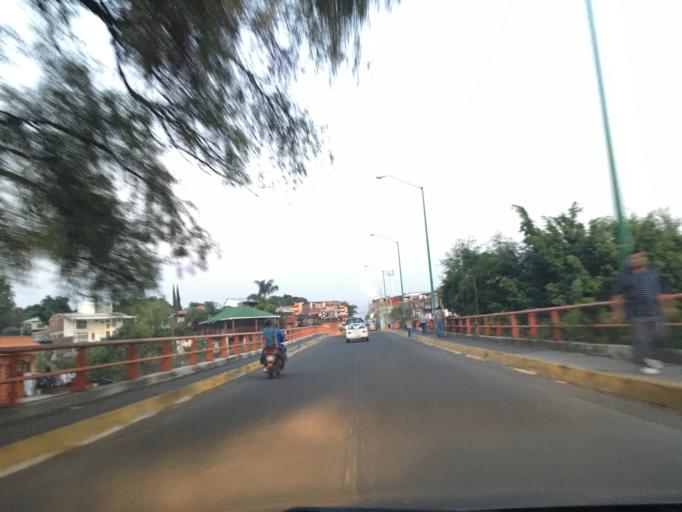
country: MX
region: Michoacan
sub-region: Uruapan
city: Uruapan
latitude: 19.4112
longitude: -102.0605
